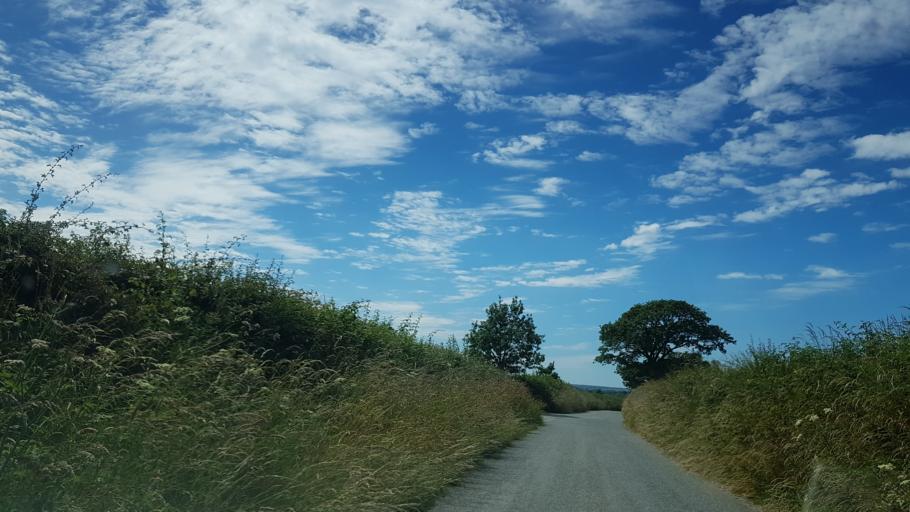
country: GB
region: Wales
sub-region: Pembrokeshire
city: Wiston
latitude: 51.8210
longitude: -4.9190
